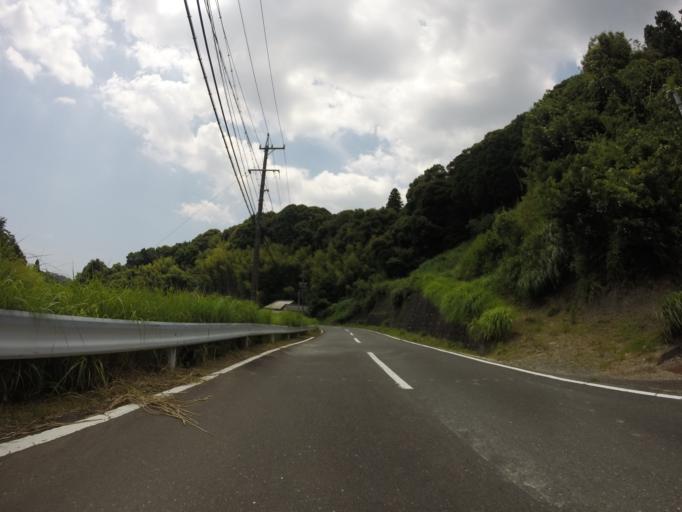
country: JP
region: Shizuoka
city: Kanaya
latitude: 34.8344
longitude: 138.0749
